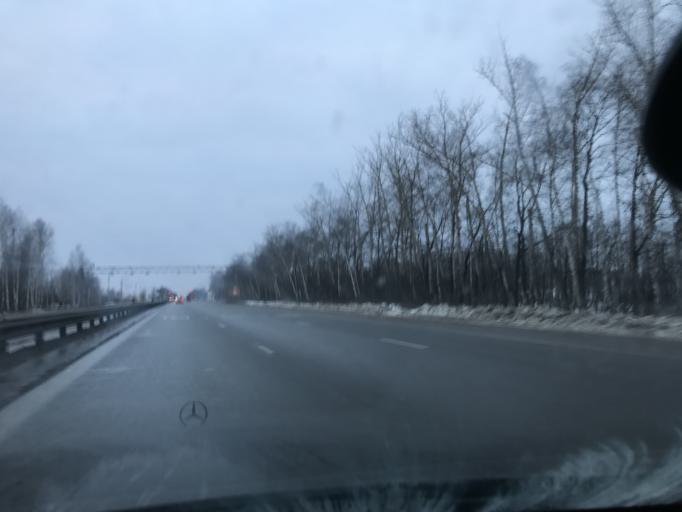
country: RU
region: Vladimir
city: Vorsha
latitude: 56.0628
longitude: 40.1318
